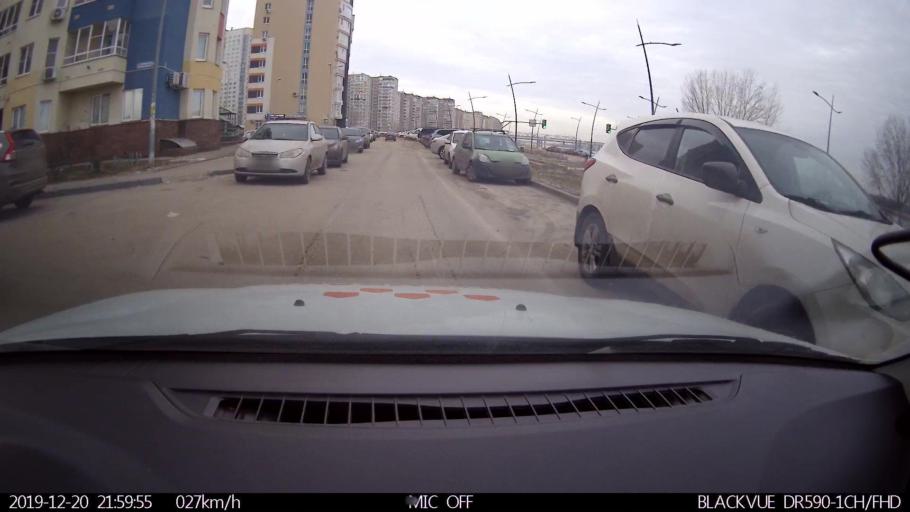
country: RU
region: Nizjnij Novgorod
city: Nizhniy Novgorod
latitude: 56.3429
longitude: 43.9507
